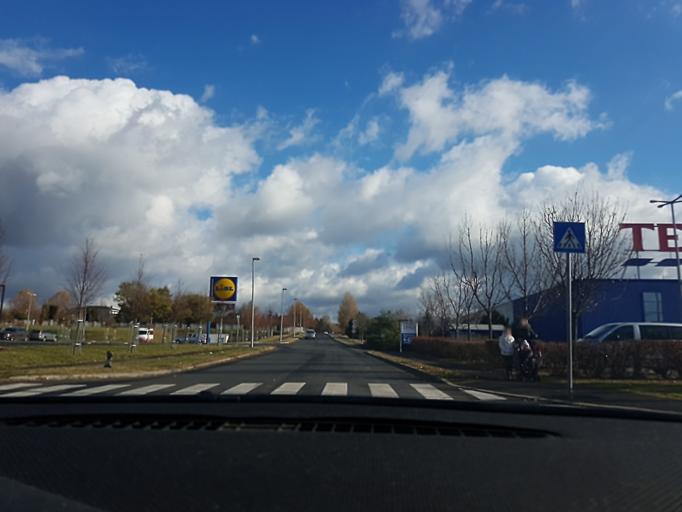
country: HU
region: Pest
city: Godollo
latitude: 47.6109
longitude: 19.3368
